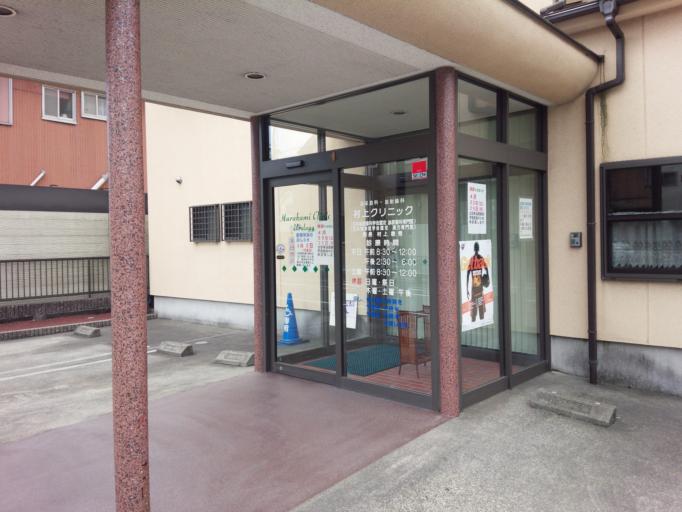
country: JP
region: Shizuoka
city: Shizuoka-shi
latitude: 35.0128
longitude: 138.4814
